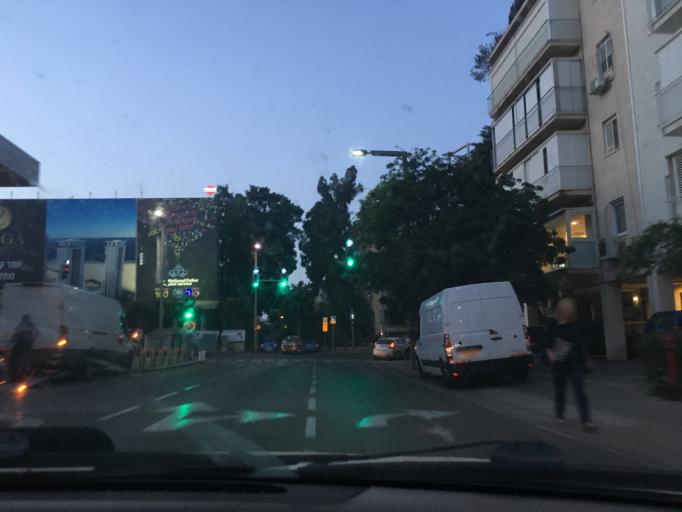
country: IL
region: Tel Aviv
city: Tel Aviv
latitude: 32.0734
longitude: 34.7805
